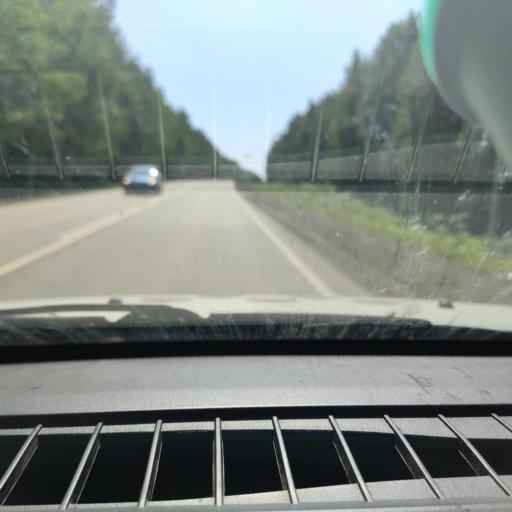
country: RU
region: Perm
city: Okhansk
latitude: 57.7891
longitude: 55.1820
